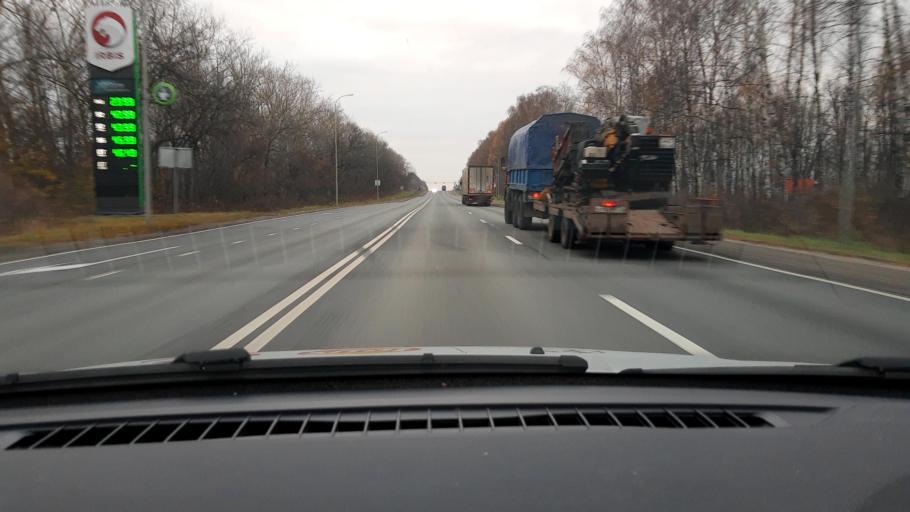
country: RU
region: Nizjnij Novgorod
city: Pamyat' Parizhskoy Kommuny
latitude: 56.0593
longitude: 44.3912
